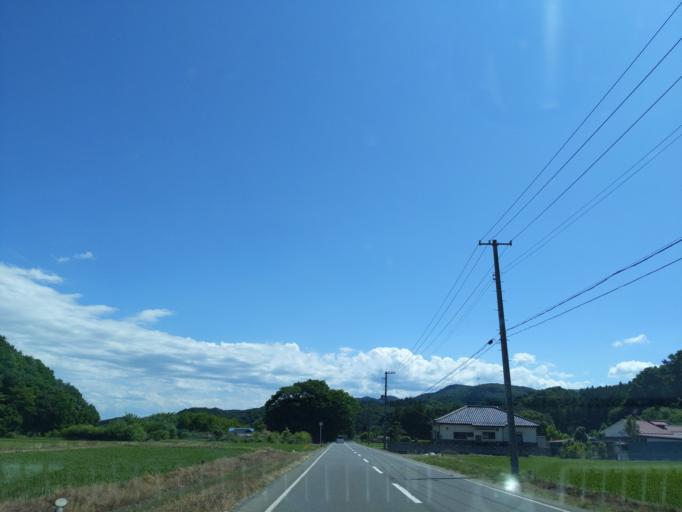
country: JP
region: Fukushima
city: Koriyama
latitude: 37.3894
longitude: 140.2631
